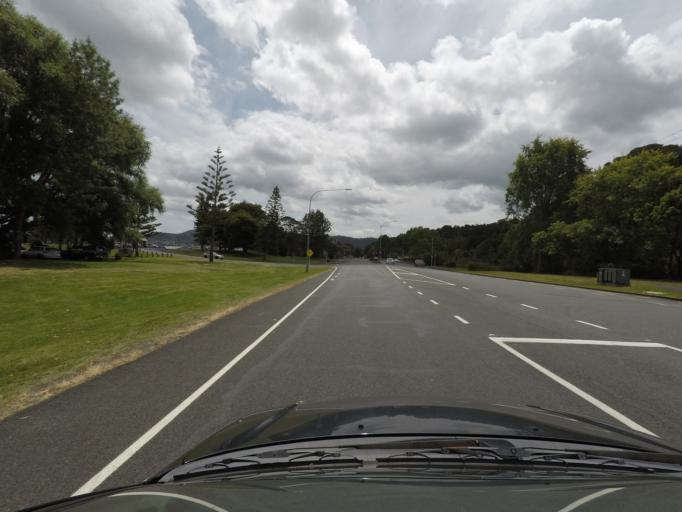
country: NZ
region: Northland
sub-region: Whangarei
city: Whangarei
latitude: -35.7290
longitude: 174.3378
